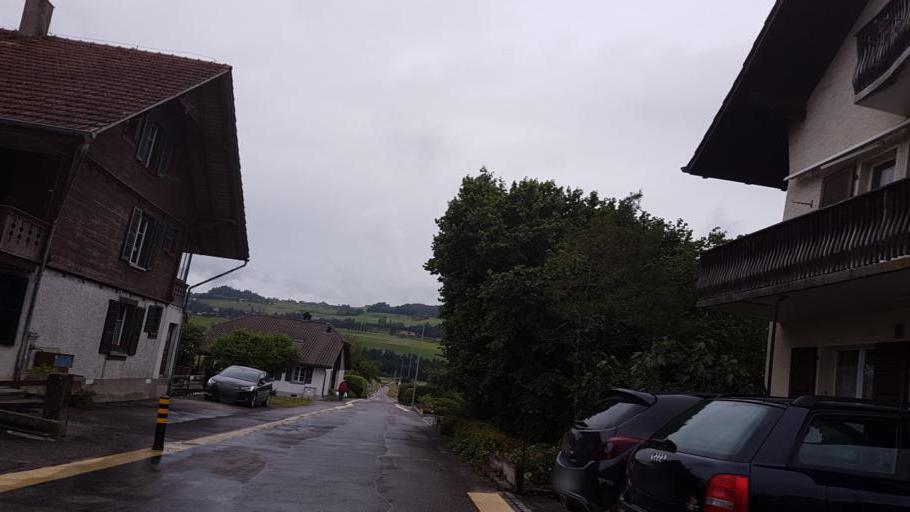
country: CH
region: Bern
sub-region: Bern-Mittelland District
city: Niederwichtrach
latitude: 46.8495
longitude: 7.5748
